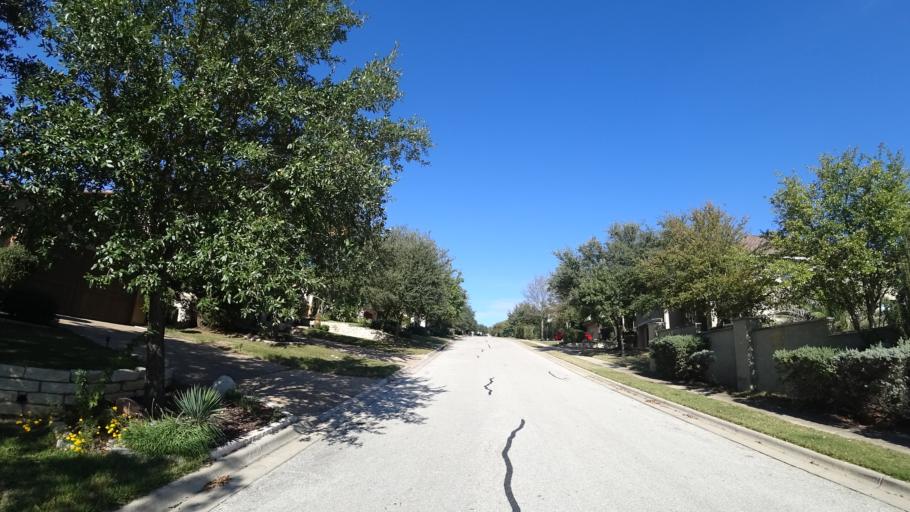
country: US
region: Texas
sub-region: Travis County
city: Hudson Bend
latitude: 30.3580
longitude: -97.8859
